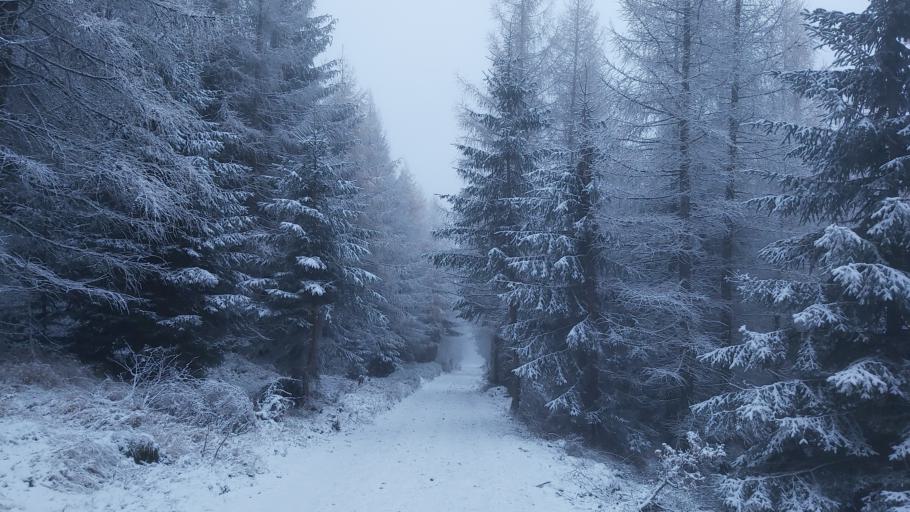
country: PL
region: Lower Silesian Voivodeship
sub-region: Powiat lubanski
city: Swieradow-Zdroj
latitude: 50.8938
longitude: 15.3387
